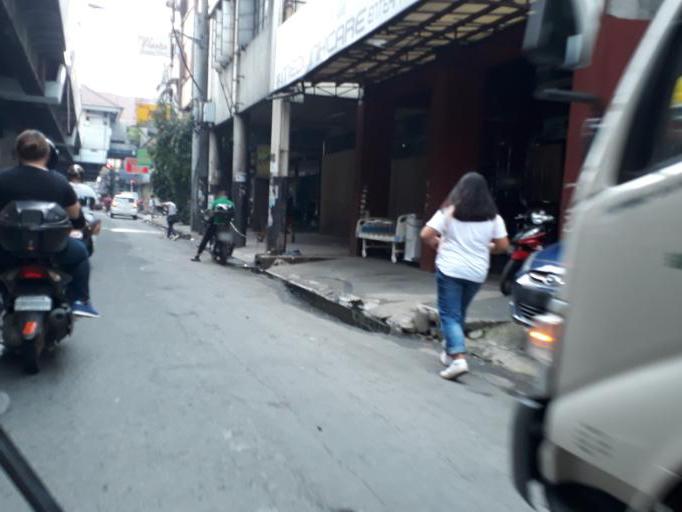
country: PH
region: Metro Manila
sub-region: City of Manila
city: Manila
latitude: 14.6098
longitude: 120.9825
